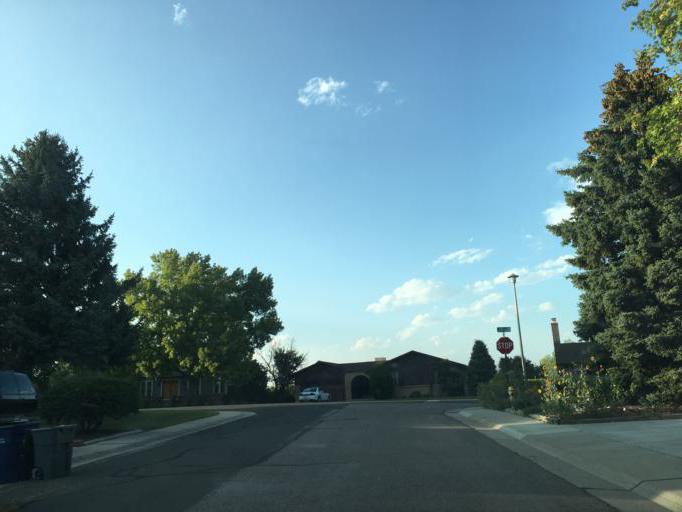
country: US
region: Colorado
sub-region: Jefferson County
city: Applewood
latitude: 39.7940
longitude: -105.1514
